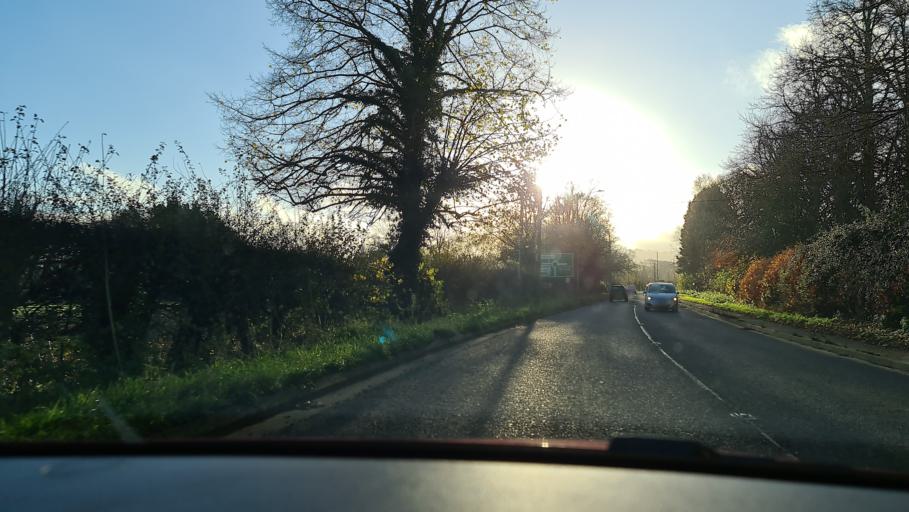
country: GB
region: England
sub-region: Buckinghamshire
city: Weston Turville
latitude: 51.7676
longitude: -0.7867
